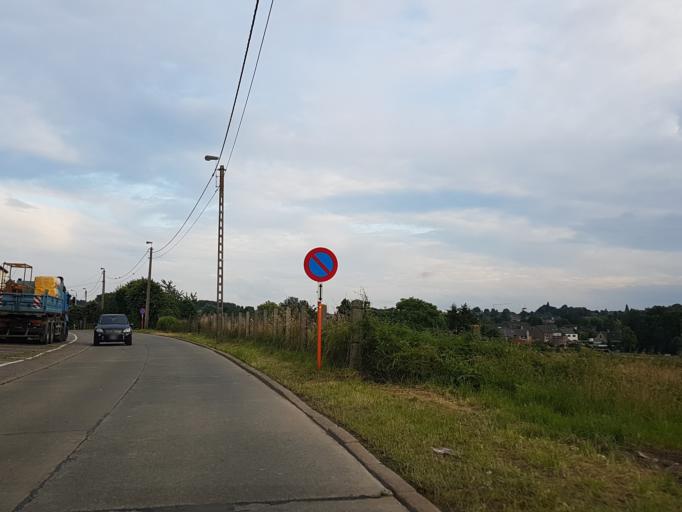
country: BE
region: Flanders
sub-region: Provincie Oost-Vlaanderen
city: Denderleeuw
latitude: 50.9239
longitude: 4.1130
